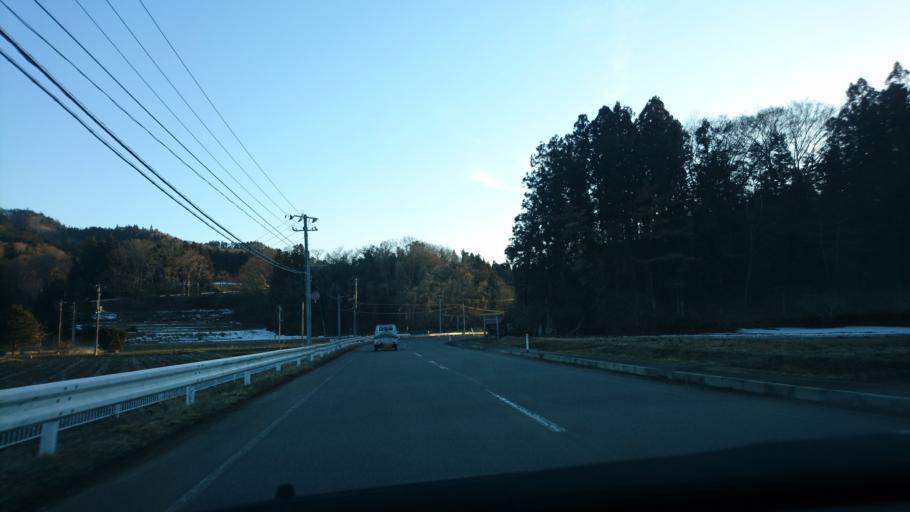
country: JP
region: Iwate
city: Mizusawa
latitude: 39.0430
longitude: 141.3529
